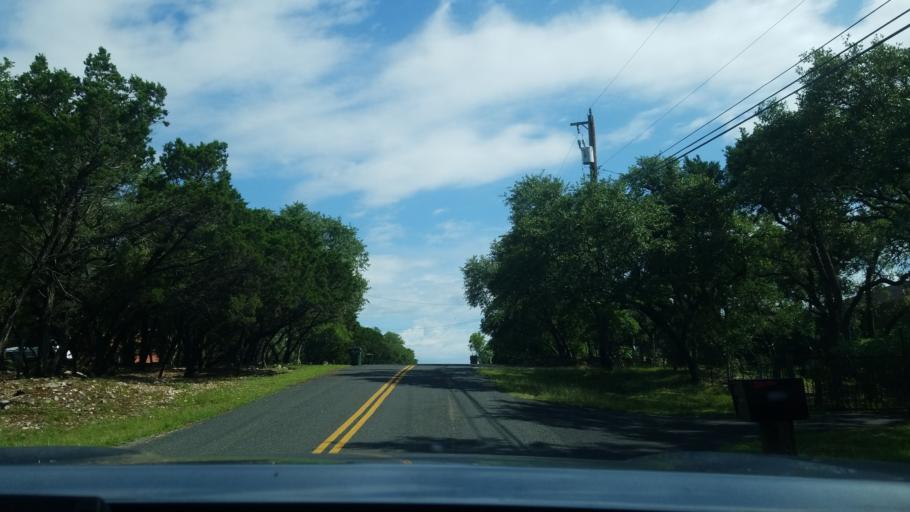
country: US
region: Texas
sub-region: Comal County
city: Bulverde
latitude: 29.7624
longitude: -98.4420
